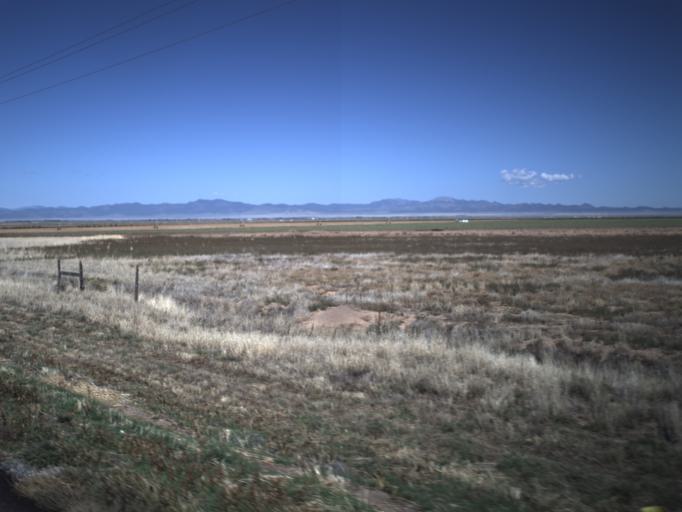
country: US
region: Utah
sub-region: Washington County
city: Enterprise
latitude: 37.6763
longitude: -113.5641
